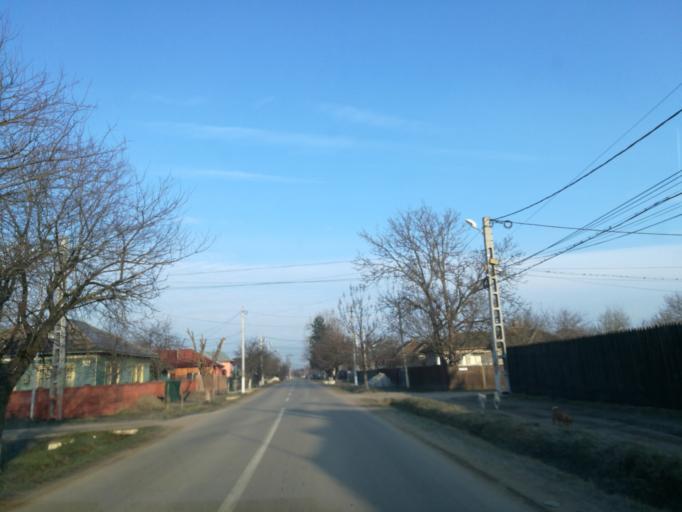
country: RO
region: Ialomita
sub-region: Comuna Fierbinti-Targ
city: Fierbintii de Jos
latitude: 44.6937
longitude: 26.3954
